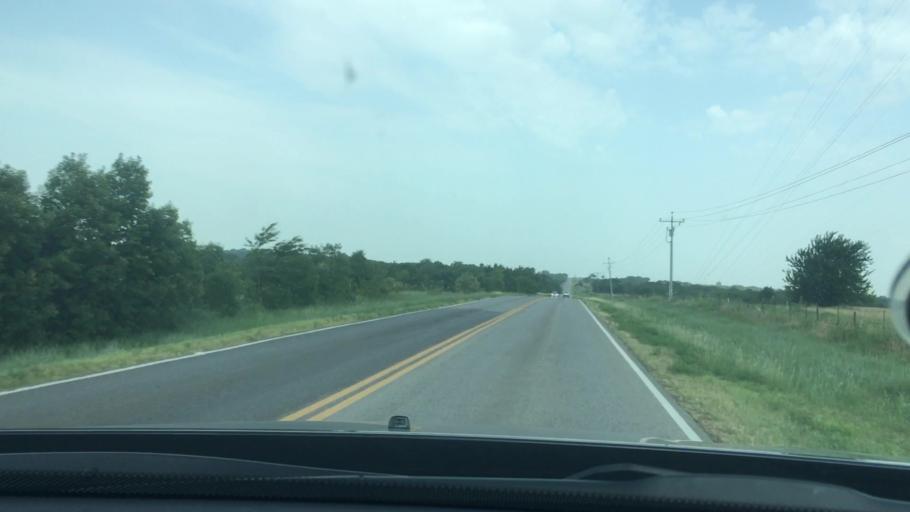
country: US
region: Oklahoma
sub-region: Garvin County
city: Stratford
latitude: 34.7967
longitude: -96.8825
